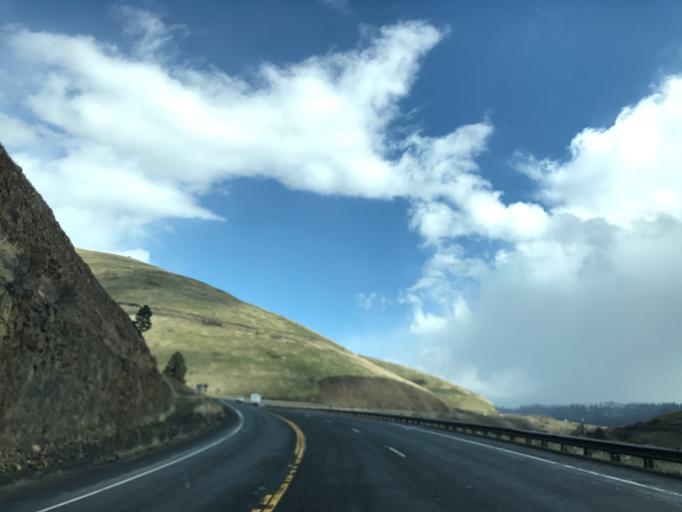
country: US
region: Idaho
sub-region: Idaho County
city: Grangeville
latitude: 45.8263
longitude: -116.2558
